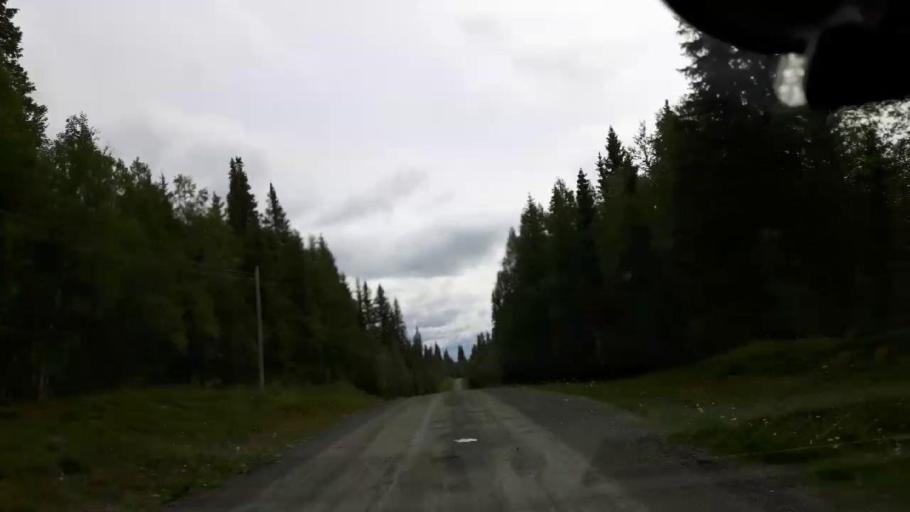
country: SE
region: Jaemtland
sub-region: Krokoms Kommun
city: Valla
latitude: 63.7221
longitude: 13.8519
